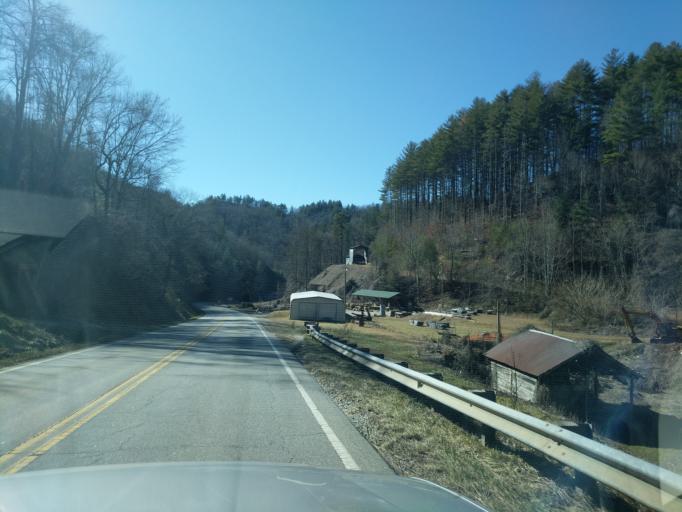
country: US
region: North Carolina
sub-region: Swain County
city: Bryson City
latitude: 35.3309
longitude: -83.5764
